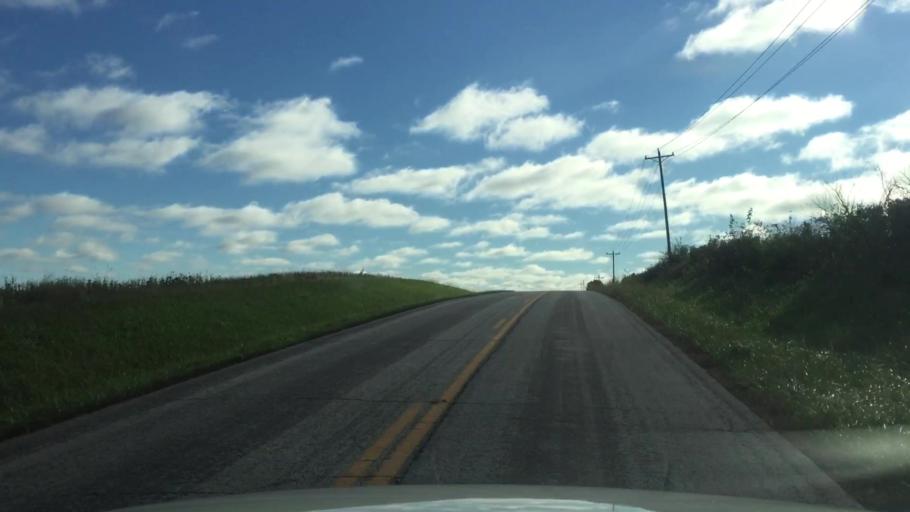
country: US
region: Missouri
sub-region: Howard County
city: Fayette
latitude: 39.1044
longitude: -92.7405
